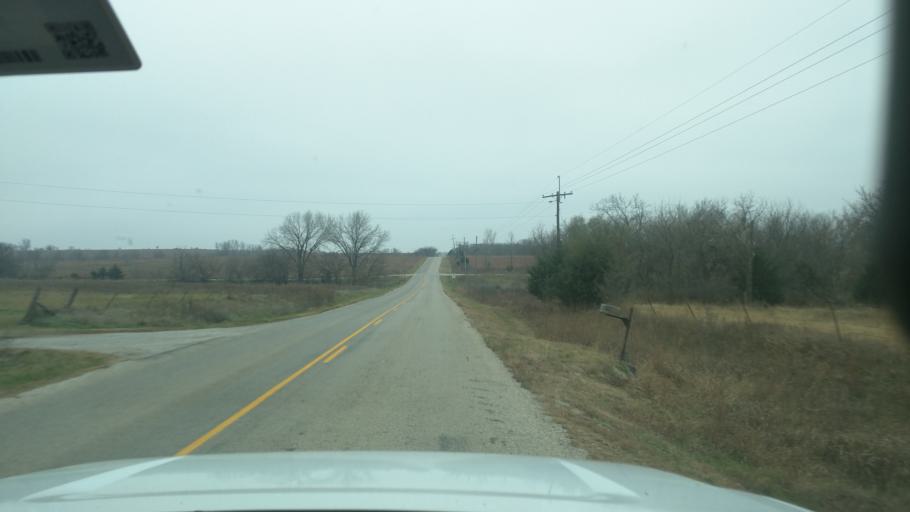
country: US
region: Kansas
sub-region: Lyon County
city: Emporia
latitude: 38.6102
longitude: -96.2610
